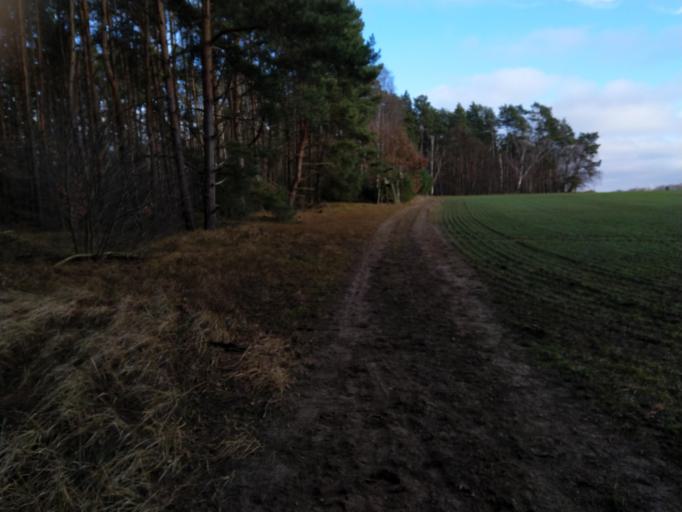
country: DE
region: Brandenburg
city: Bernau bei Berlin
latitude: 52.6302
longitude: 13.6337
